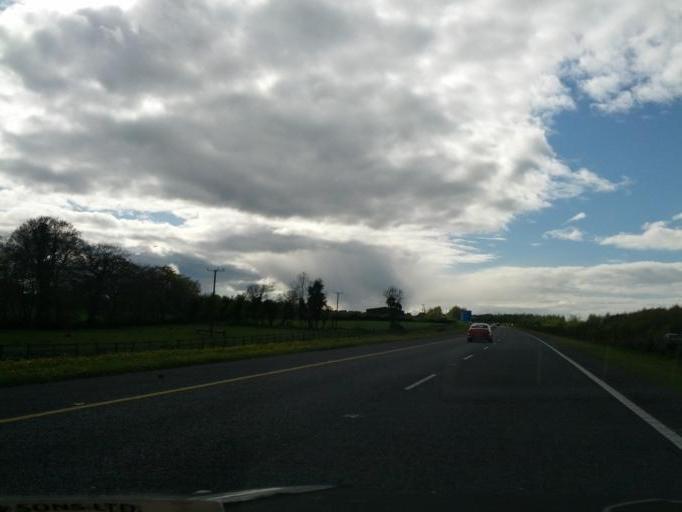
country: IE
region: Leinster
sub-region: Kildare
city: Kilcock
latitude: 53.4087
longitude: -6.7121
